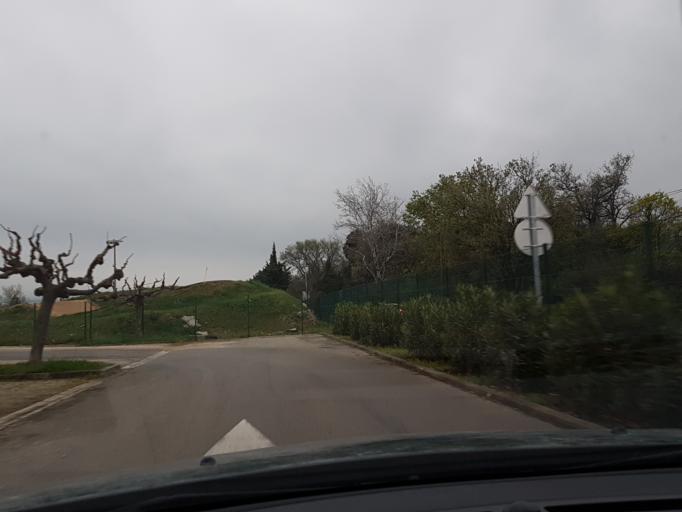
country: FR
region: Provence-Alpes-Cote d'Azur
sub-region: Departement du Vaucluse
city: Carpentras
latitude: 44.0429
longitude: 5.0543
